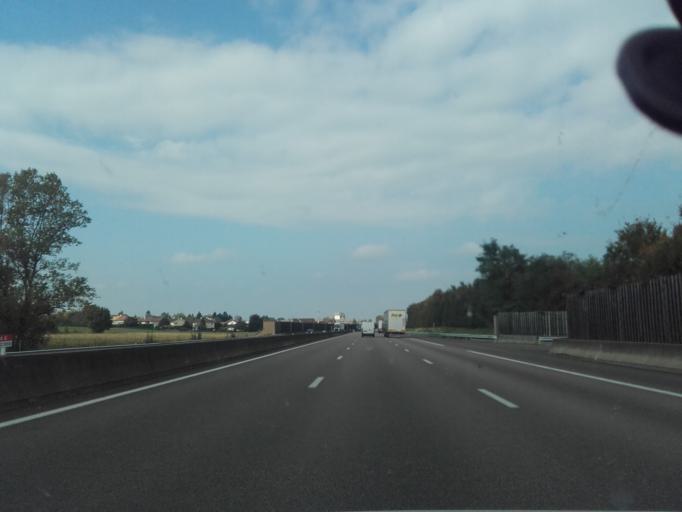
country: FR
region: Bourgogne
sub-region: Departement de Saone-et-Loire
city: Saint-Remy
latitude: 46.7697
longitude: 4.8216
